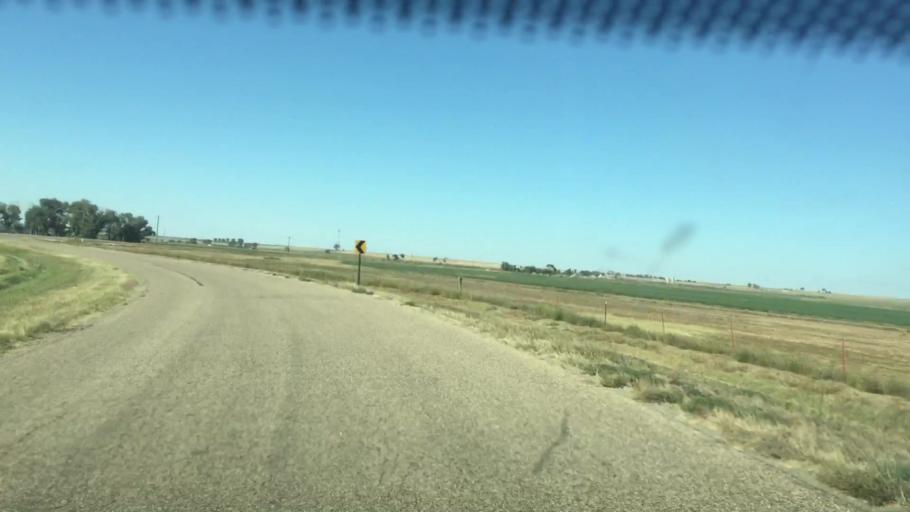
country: US
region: Colorado
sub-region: Prowers County
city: Lamar
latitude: 38.0987
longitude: -102.5196
